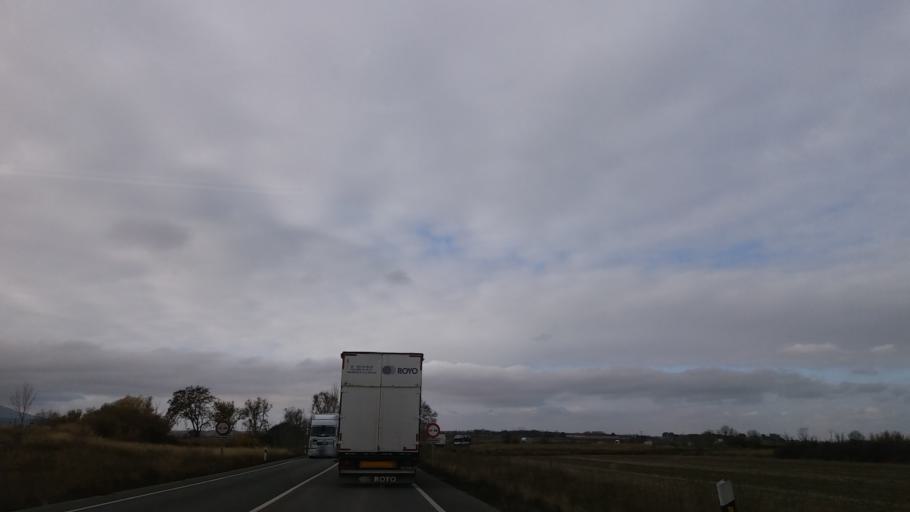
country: ES
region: Aragon
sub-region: Provincia de Zaragoza
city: Mallen
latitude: 41.9094
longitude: -1.4282
